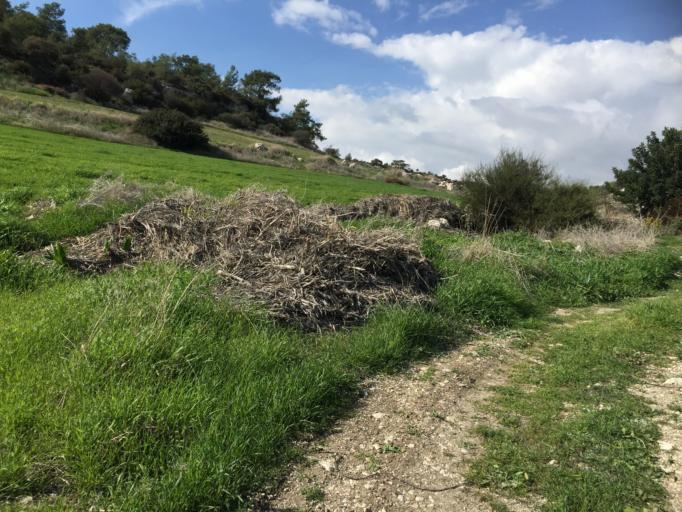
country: CY
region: Larnaka
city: Agios Tychon
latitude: 34.7418
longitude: 33.1407
